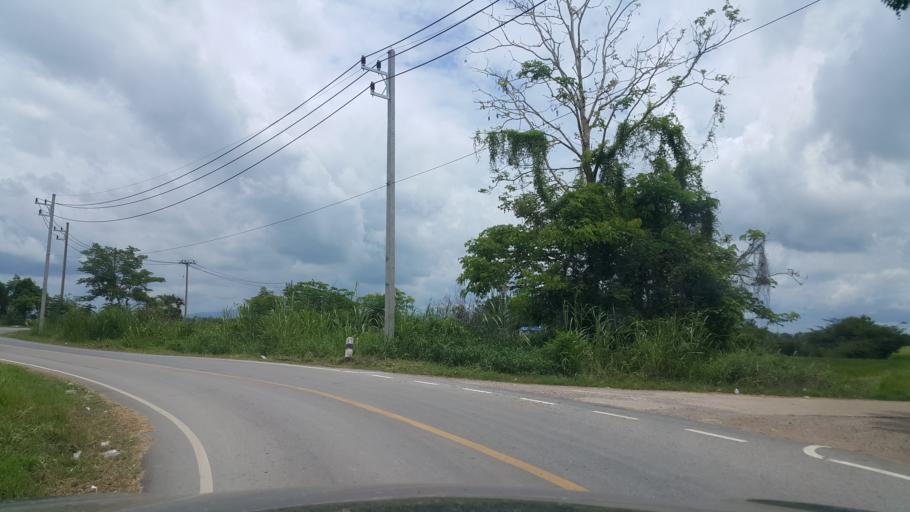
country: TH
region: Sukhothai
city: Kong Krailat
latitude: 16.9342
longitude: 99.9554
